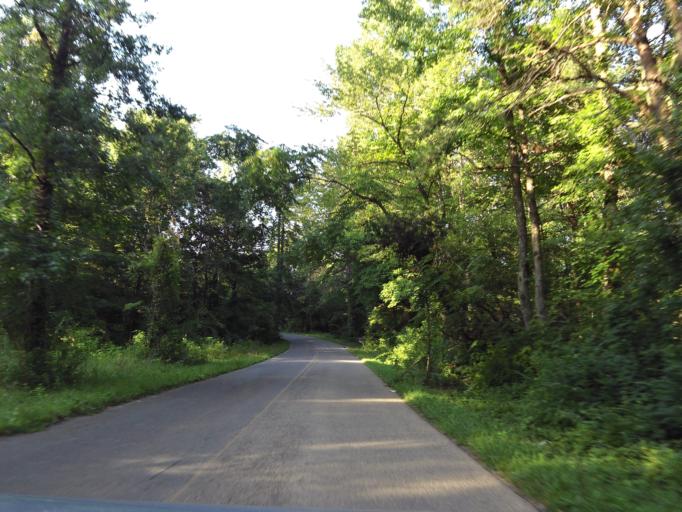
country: US
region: Tennessee
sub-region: Blount County
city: Maryville
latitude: 35.6182
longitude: -83.9403
